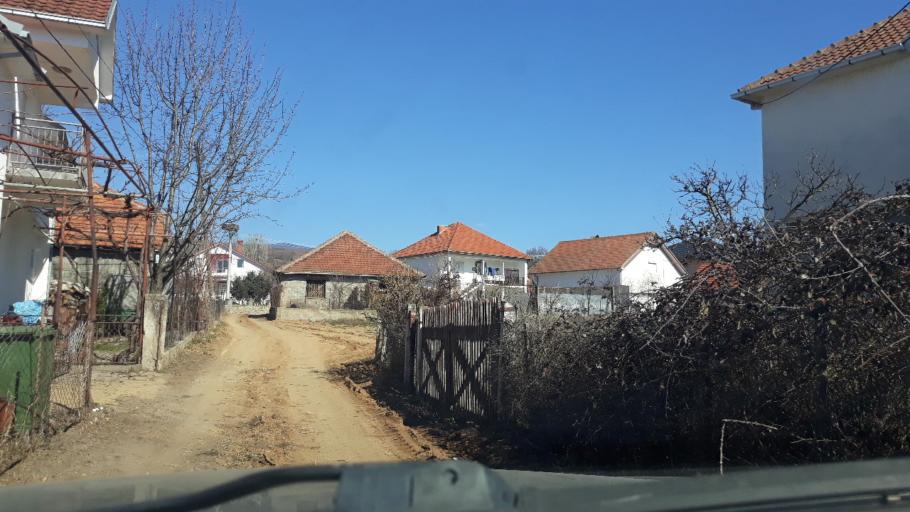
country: MK
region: Novo Selo
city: Novo Selo
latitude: 41.4171
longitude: 22.8758
